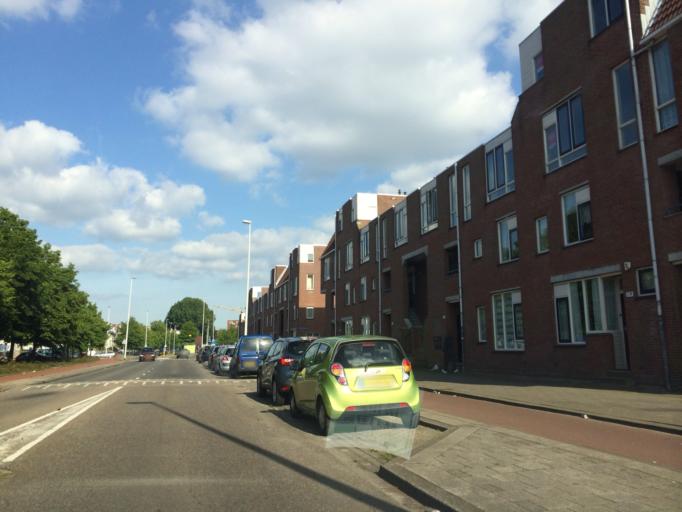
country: NL
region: South Holland
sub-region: Gemeente Rotterdam
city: Rotterdam
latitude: 51.9260
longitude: 4.5019
